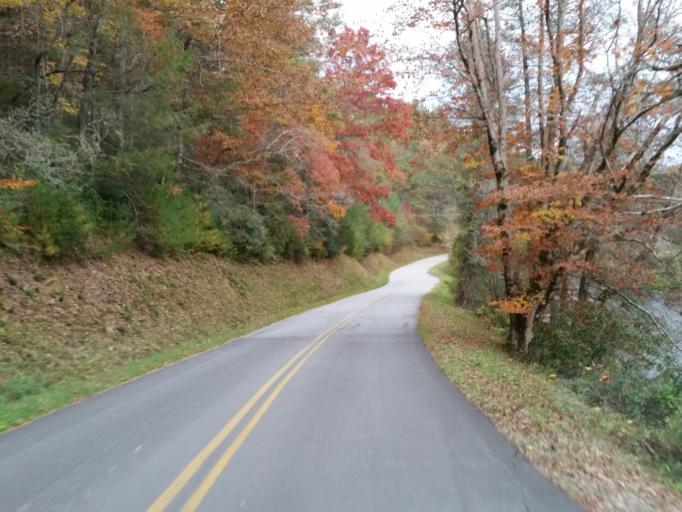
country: US
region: Georgia
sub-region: Fannin County
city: Blue Ridge
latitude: 34.7563
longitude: -84.1888
